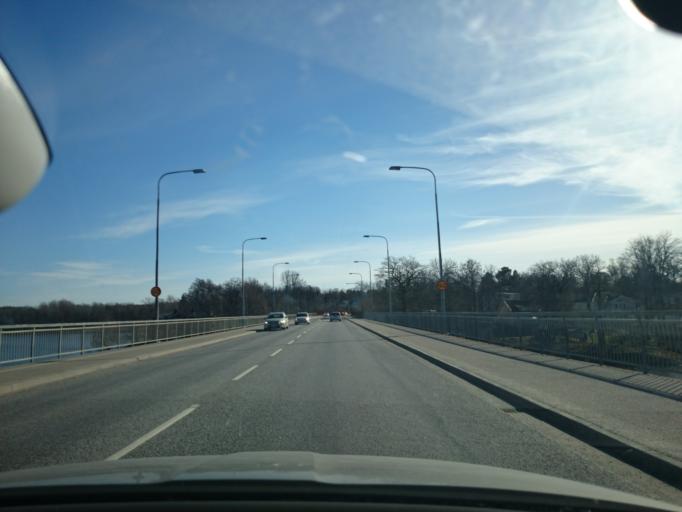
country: SE
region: Stockholm
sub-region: Stockholms Kommun
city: Arsta
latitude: 59.2316
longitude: 18.0889
